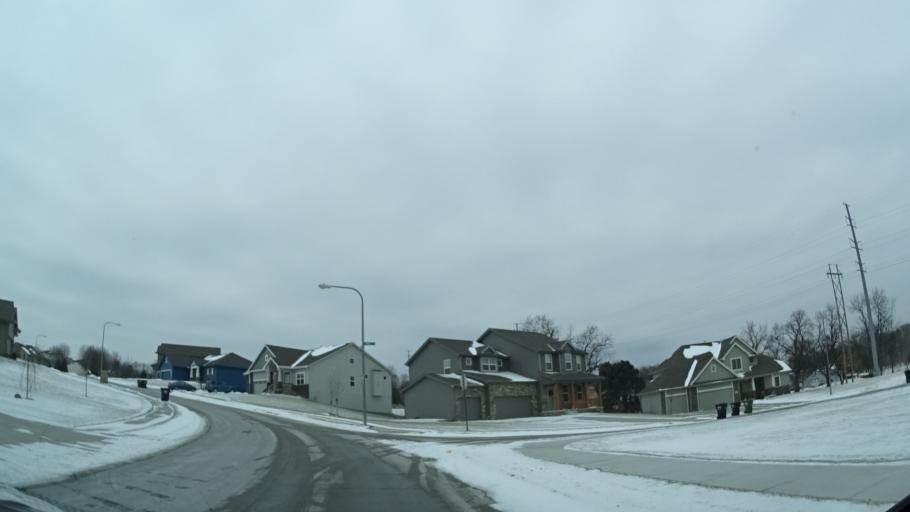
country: US
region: Nebraska
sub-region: Sarpy County
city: Offutt Air Force Base
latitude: 41.1682
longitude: -95.9456
